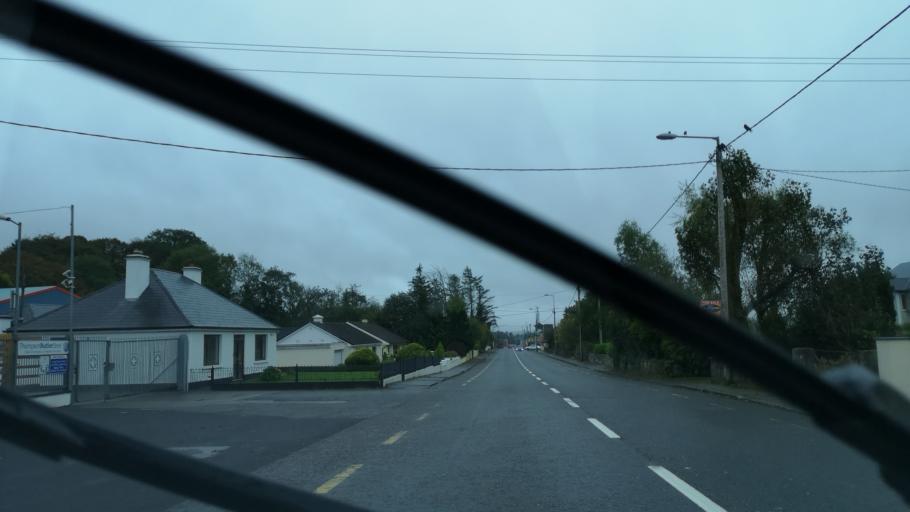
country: IE
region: Connaught
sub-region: Roscommon
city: Ballaghaderreen
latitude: 53.9048
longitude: -8.5859
